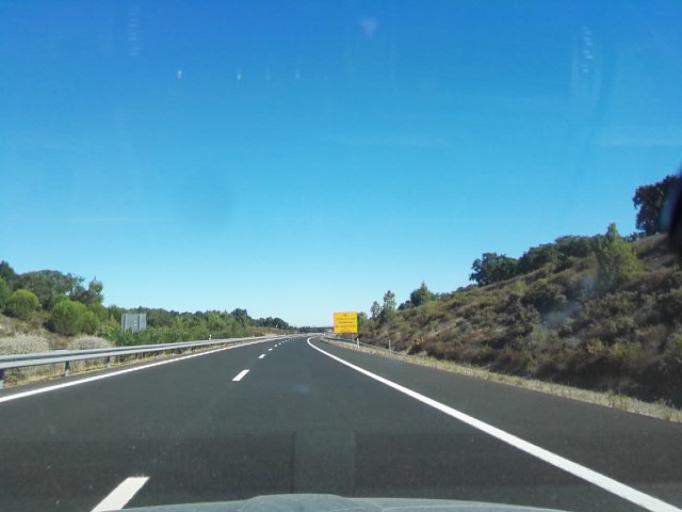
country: PT
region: Santarem
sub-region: Benavente
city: Poceirao
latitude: 38.8818
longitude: -8.7941
